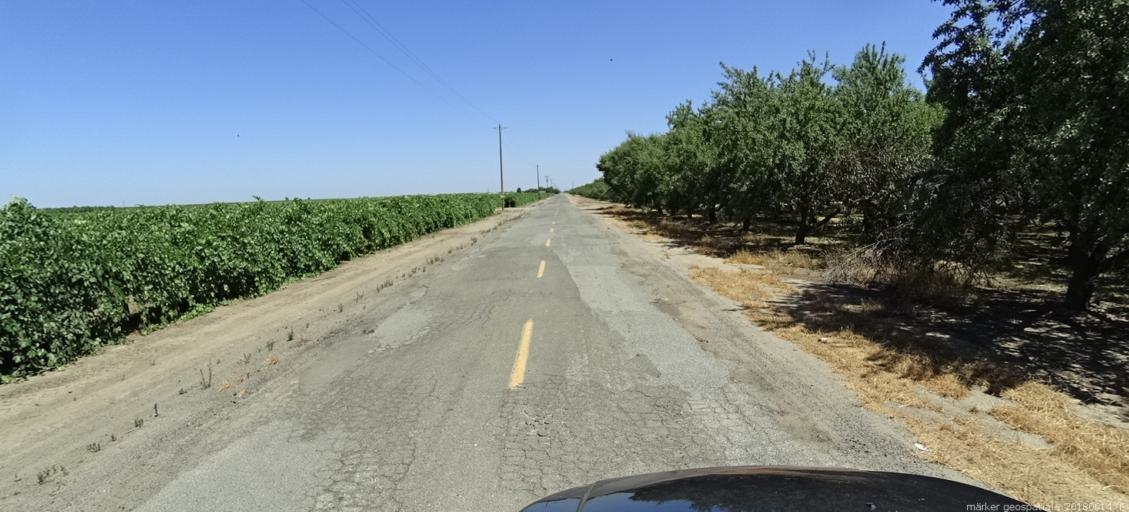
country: US
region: California
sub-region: Madera County
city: Fairmead
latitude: 37.0212
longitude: -120.2387
